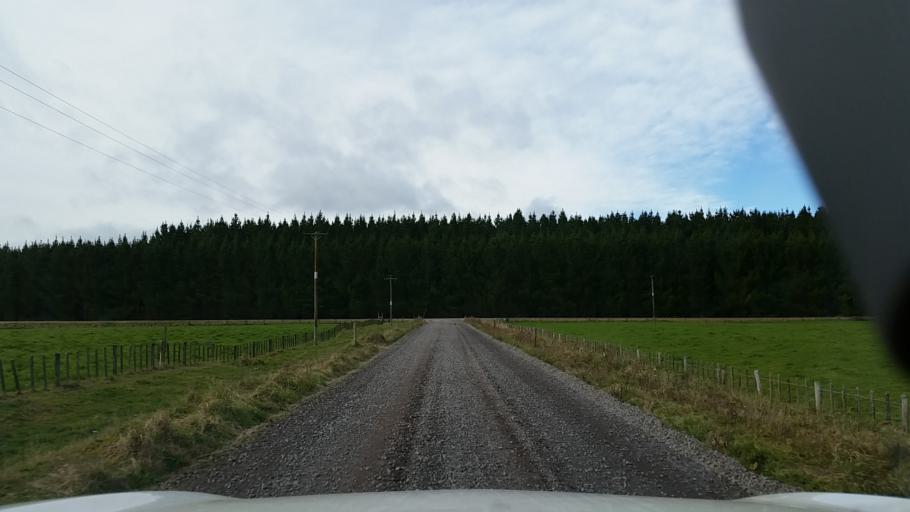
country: NZ
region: Bay of Plenty
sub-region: Whakatane District
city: Murupara
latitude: -38.4912
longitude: 176.4799
